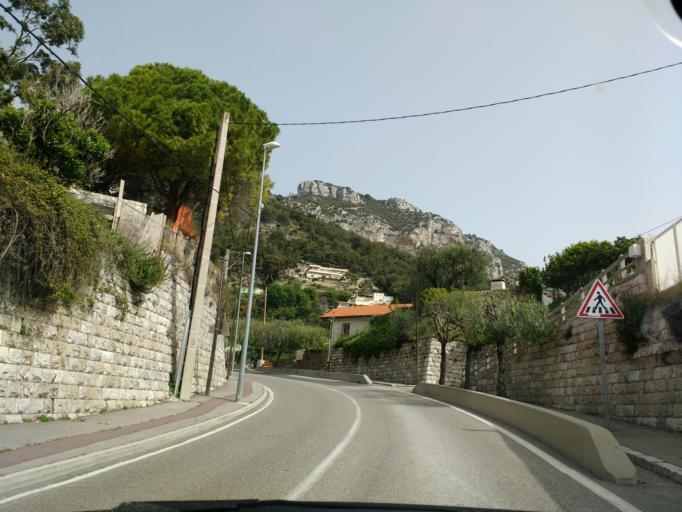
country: MC
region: Commune de Monaco
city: Saint-Roman
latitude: 43.7499
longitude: 7.4265
